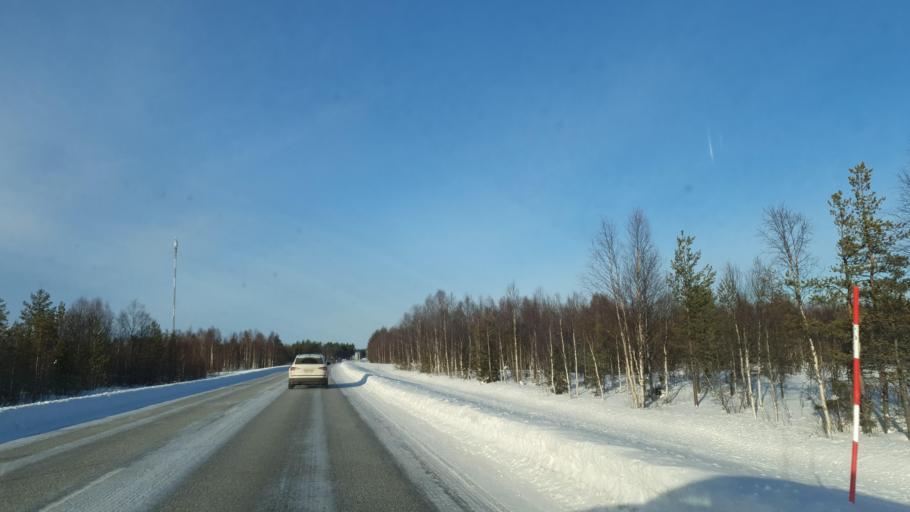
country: FI
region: Lapland
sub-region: Tunturi-Lappi
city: Kolari
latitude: 67.3276
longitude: 23.8220
